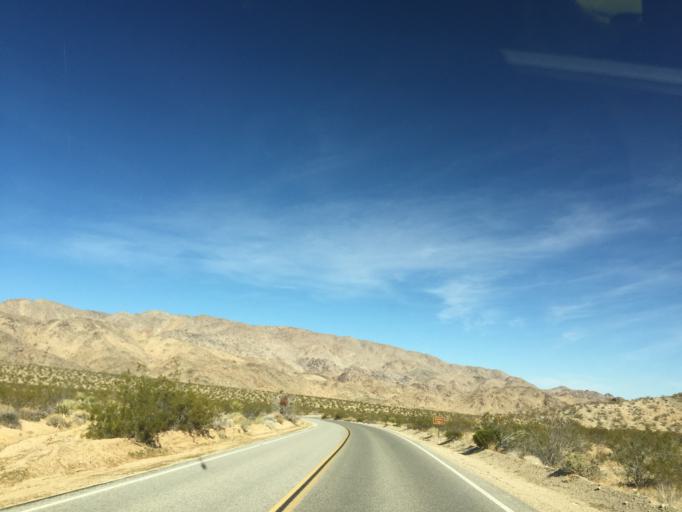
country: US
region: California
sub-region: San Bernardino County
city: Twentynine Palms
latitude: 34.0399
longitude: -116.0234
